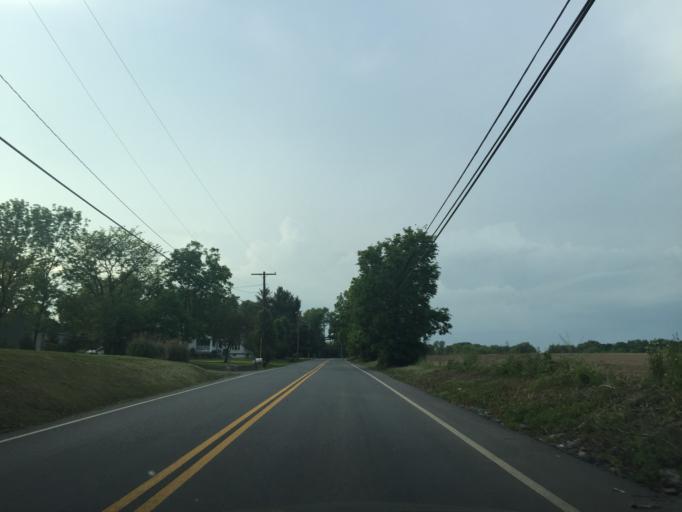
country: US
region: Maryland
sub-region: Frederick County
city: Brunswick
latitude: 39.3420
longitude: -77.6093
